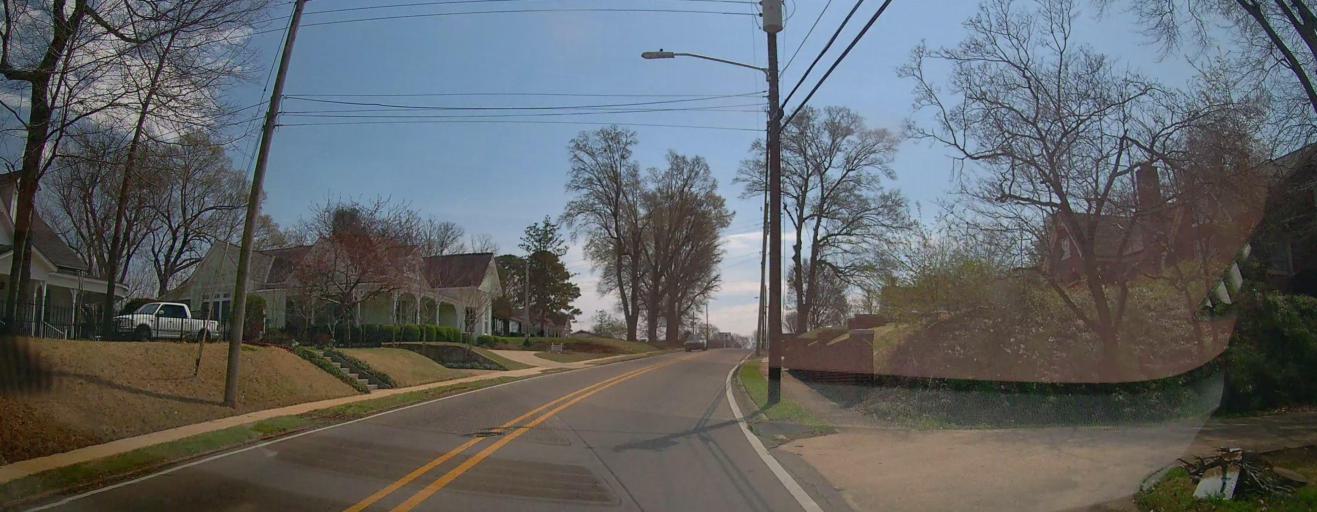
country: US
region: Mississippi
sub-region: Union County
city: New Albany
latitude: 34.4899
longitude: -89.0036
